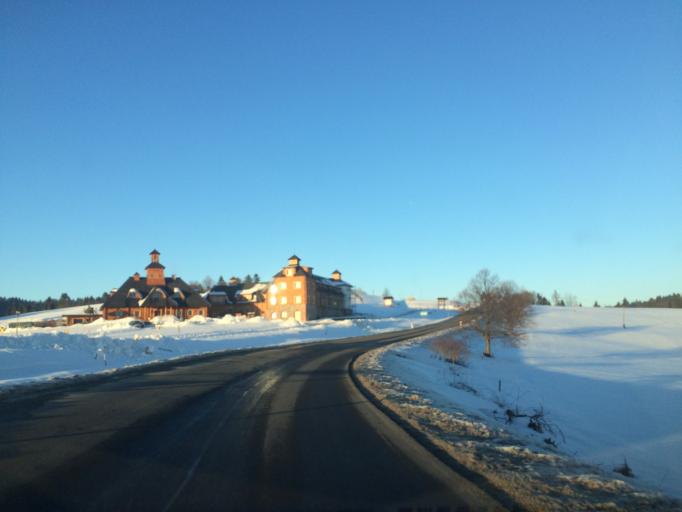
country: PL
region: Subcarpathian Voivodeship
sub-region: Powiat bieszczadzki
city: Lutowiska
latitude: 49.2622
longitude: 22.6831
